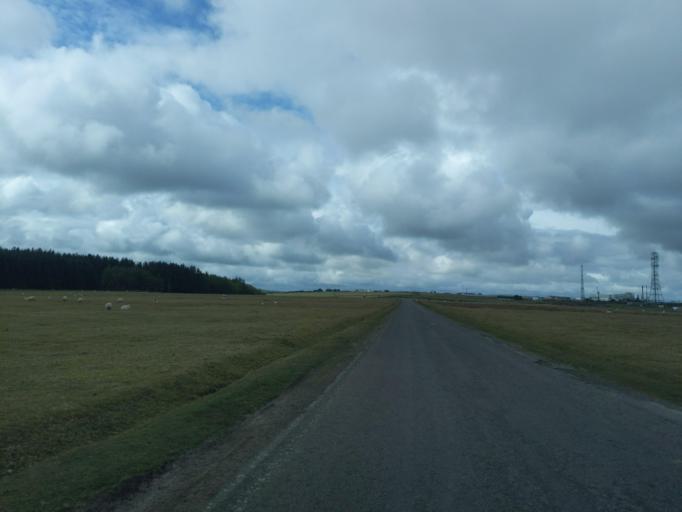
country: GB
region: England
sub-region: Cornwall
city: Camelford
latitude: 50.6374
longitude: -4.6222
